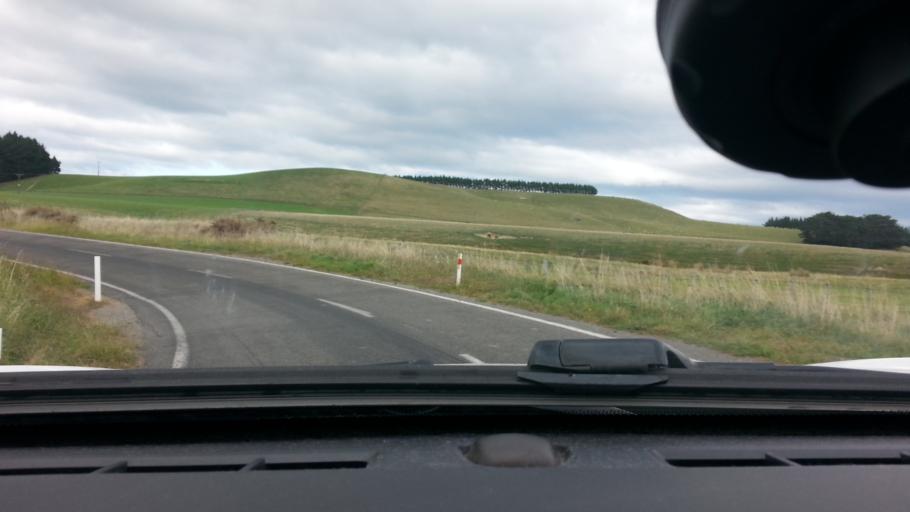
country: NZ
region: Wellington
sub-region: Upper Hutt City
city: Upper Hutt
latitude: -41.3720
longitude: 175.1744
